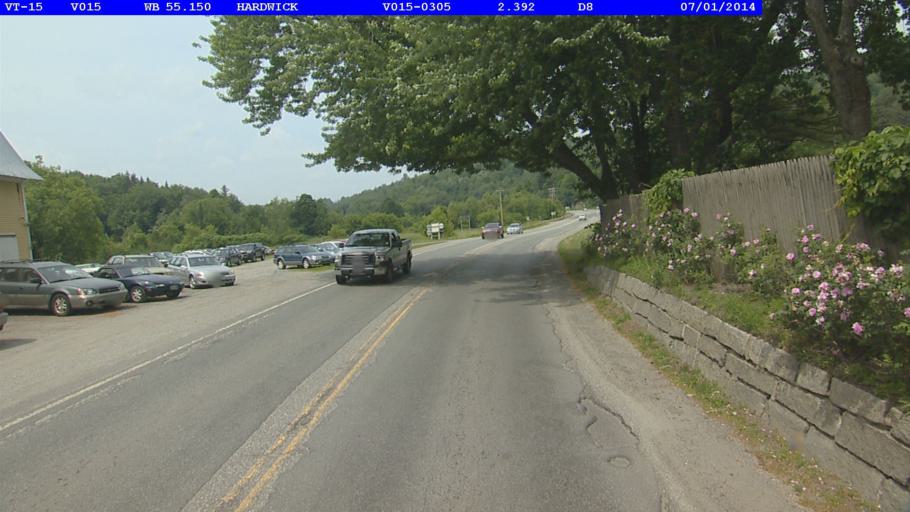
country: US
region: Vermont
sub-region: Caledonia County
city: Hardwick
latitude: 44.5159
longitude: -72.3761
